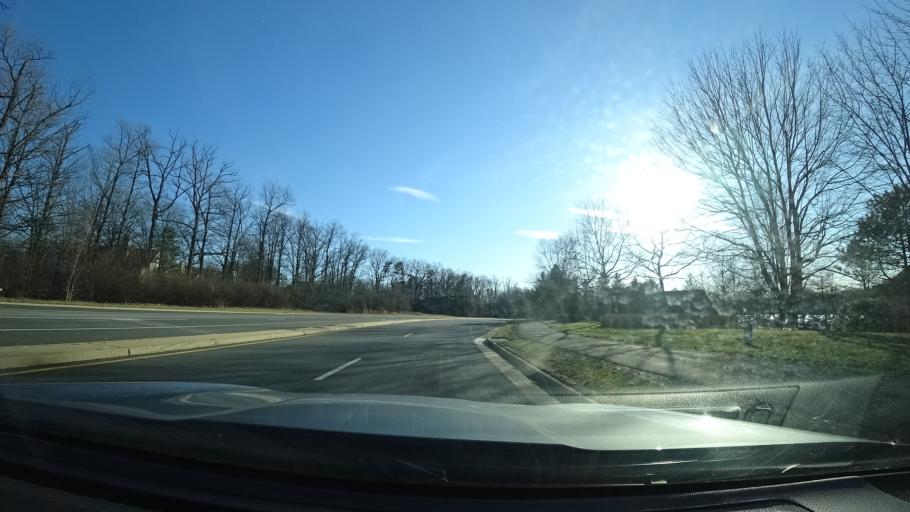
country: US
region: Virginia
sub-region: Fairfax County
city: Reston
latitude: 38.9800
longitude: -77.3476
